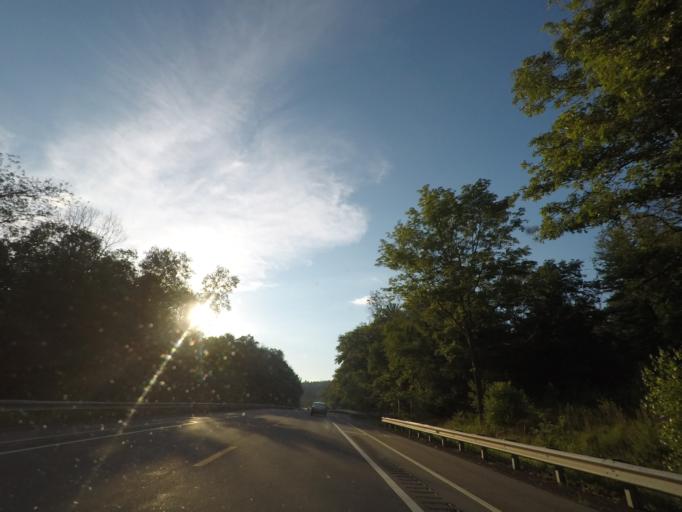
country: US
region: Massachusetts
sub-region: Hampden County
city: Brimfield
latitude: 42.1150
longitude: -72.1870
